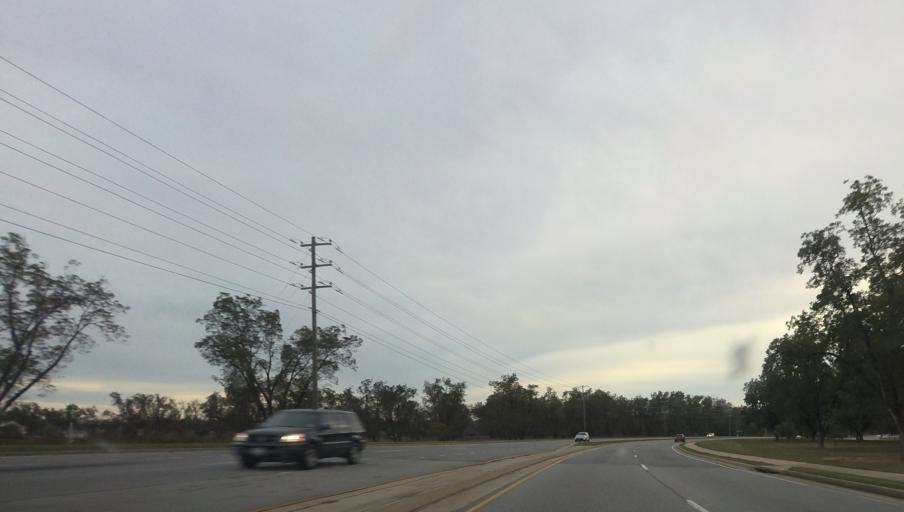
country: US
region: Georgia
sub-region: Houston County
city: Perry
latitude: 32.5014
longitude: -83.6631
